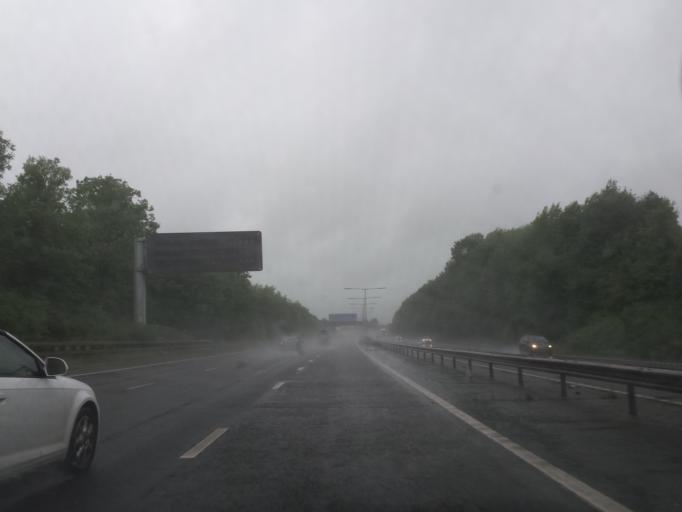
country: GB
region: England
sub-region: Warwickshire
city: Bedworth
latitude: 52.4557
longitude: -1.4178
